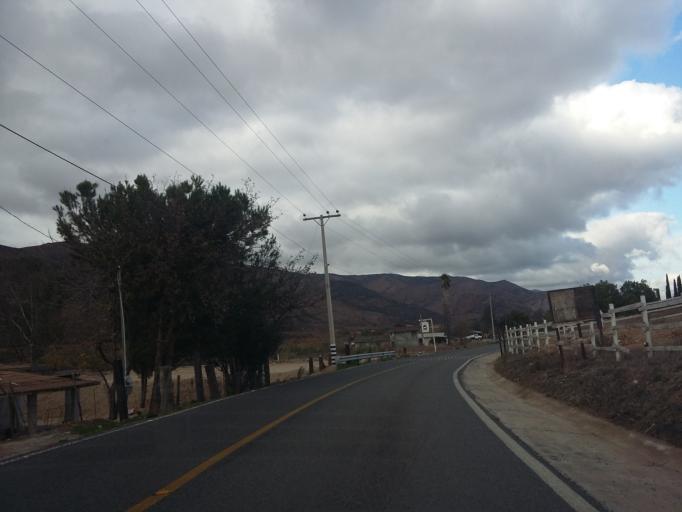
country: MX
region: Baja California
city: El Sauzal
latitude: 32.0263
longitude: -116.6742
